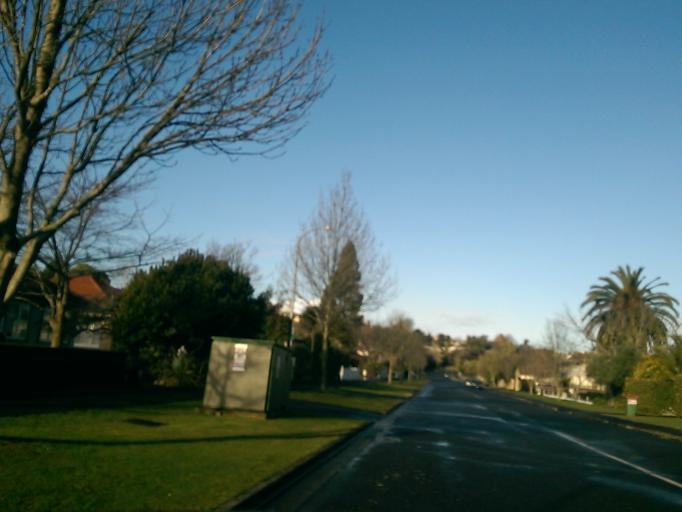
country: NZ
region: Waikato
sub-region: Hamilton City
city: Hamilton
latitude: -37.7981
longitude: 175.3114
